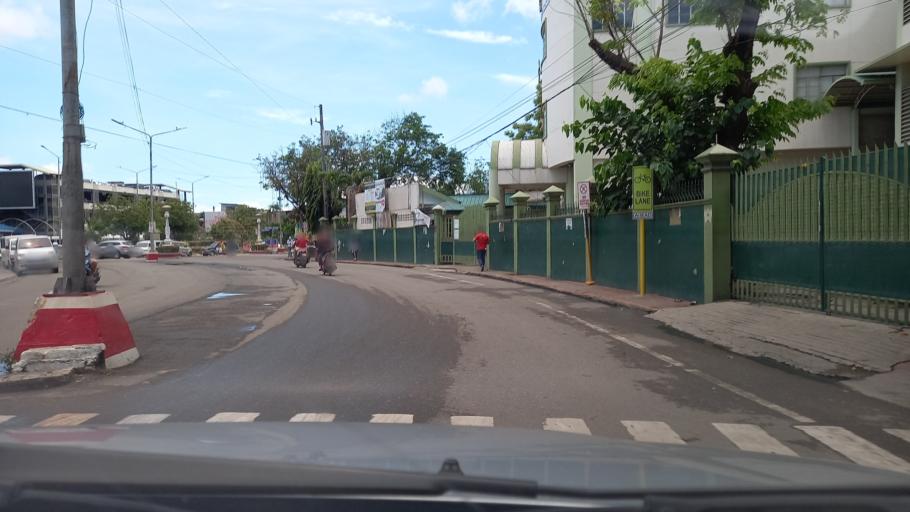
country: PH
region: Central Visayas
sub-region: Lapu-Lapu City
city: Buagsong
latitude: 10.3279
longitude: 123.9427
